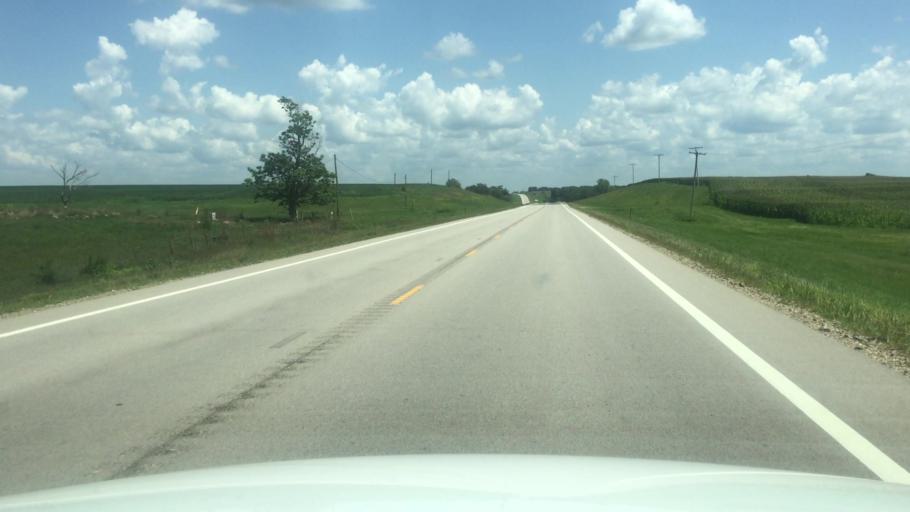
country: US
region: Kansas
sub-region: Brown County
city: Horton
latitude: 39.6674
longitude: -95.4852
